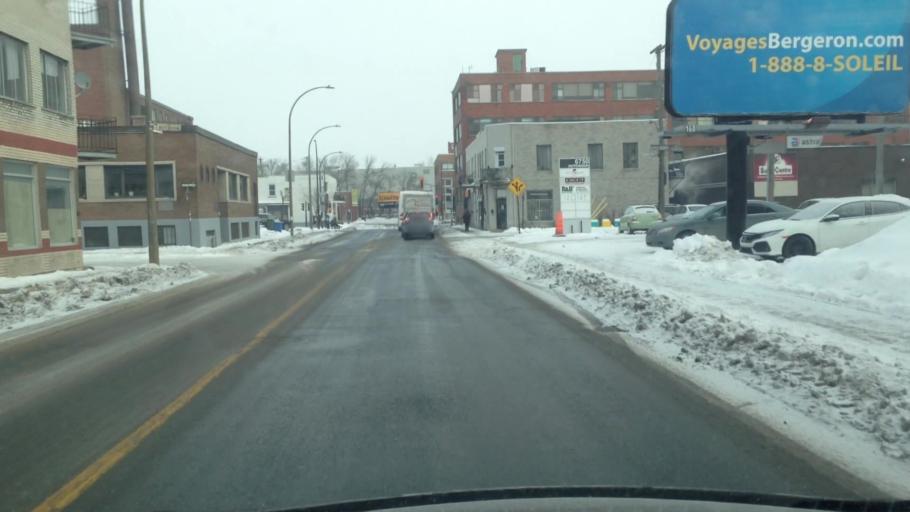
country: CA
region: Quebec
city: Mont-Royal
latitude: 45.5281
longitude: -73.6188
